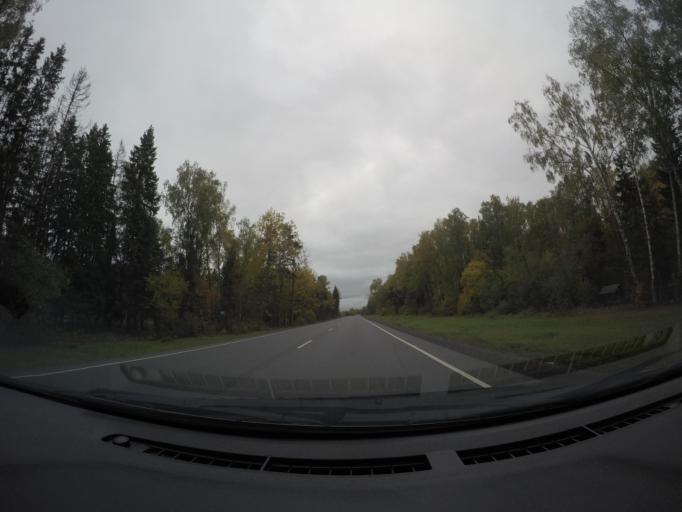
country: RU
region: Moskovskaya
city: Ruza
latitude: 55.7256
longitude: 36.2162
